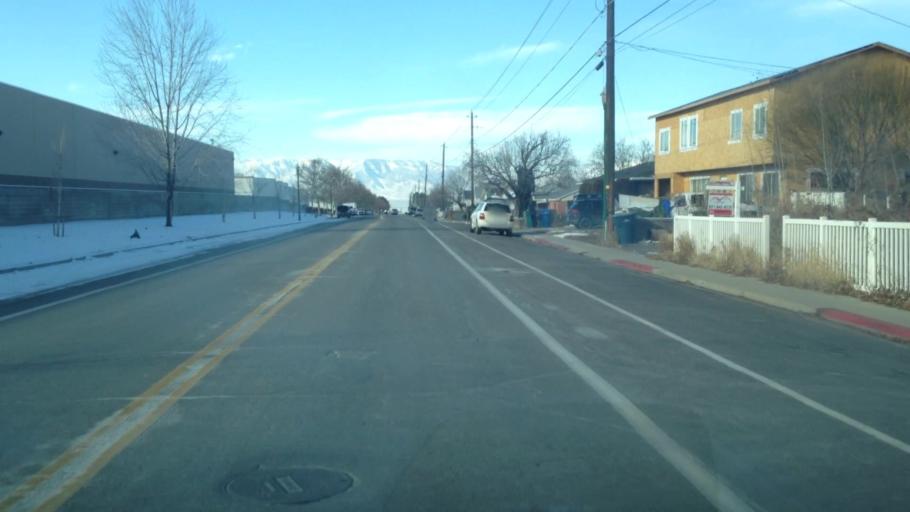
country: US
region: Utah
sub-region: Utah County
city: Orem
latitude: 40.2753
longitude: -111.6979
